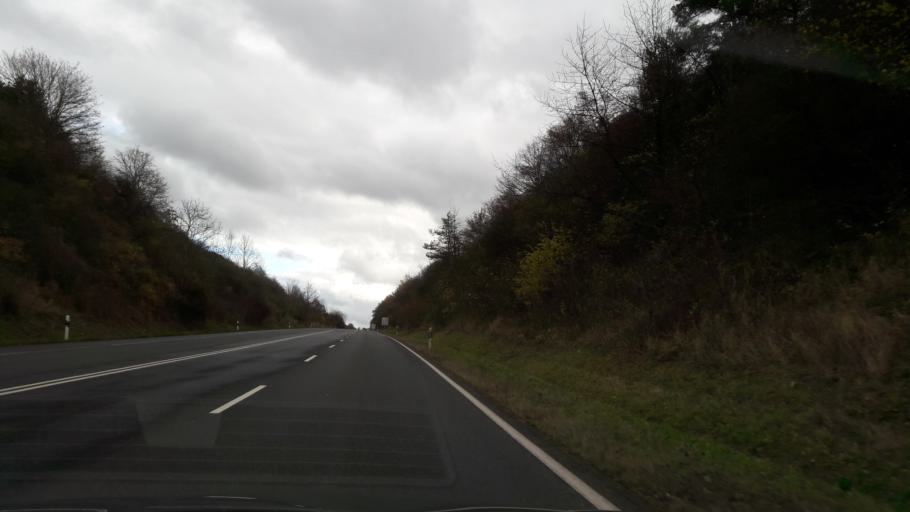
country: DE
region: Rheinland-Pfalz
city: Waldrach
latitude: 49.7674
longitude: 6.7570
